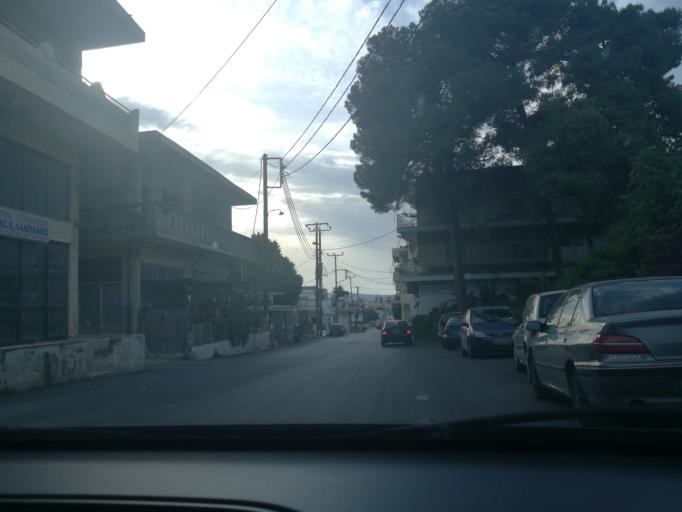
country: GR
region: Crete
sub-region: Nomos Irakleiou
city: Irakleion
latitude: 35.3161
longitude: 25.1380
